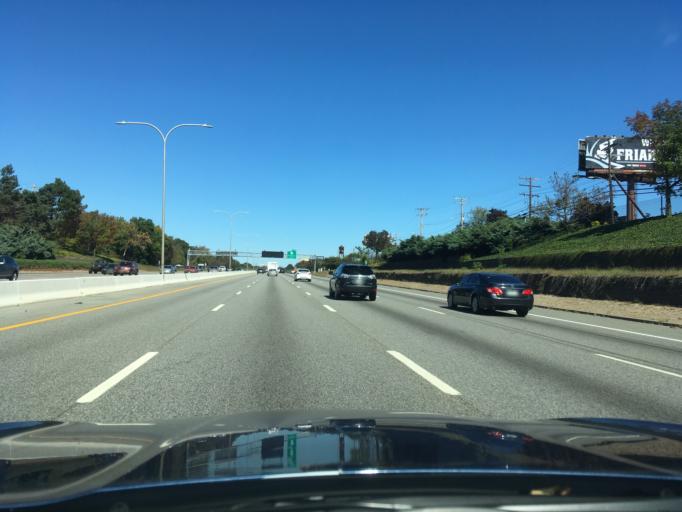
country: US
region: Rhode Island
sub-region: Providence County
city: Cranston
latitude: 41.7674
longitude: -71.4297
